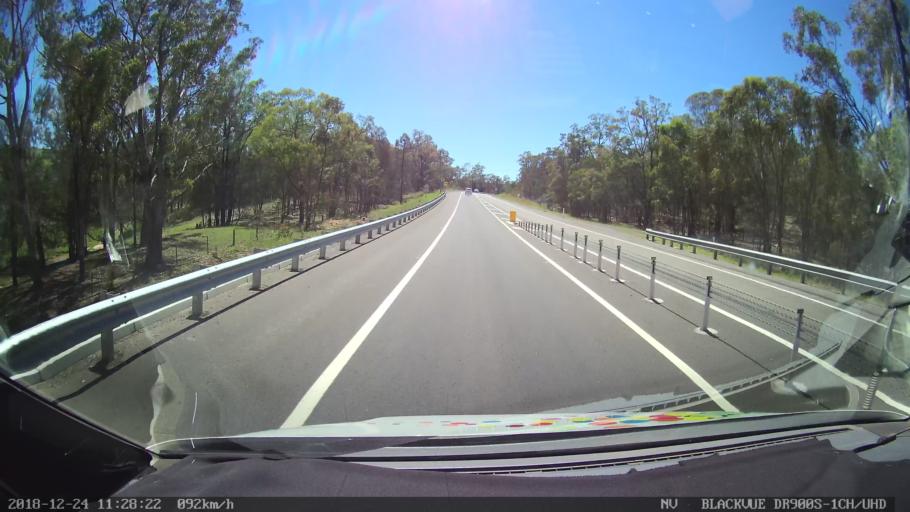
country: AU
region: New South Wales
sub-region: Upper Hunter Shire
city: Merriwa
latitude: -32.1887
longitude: 150.4464
